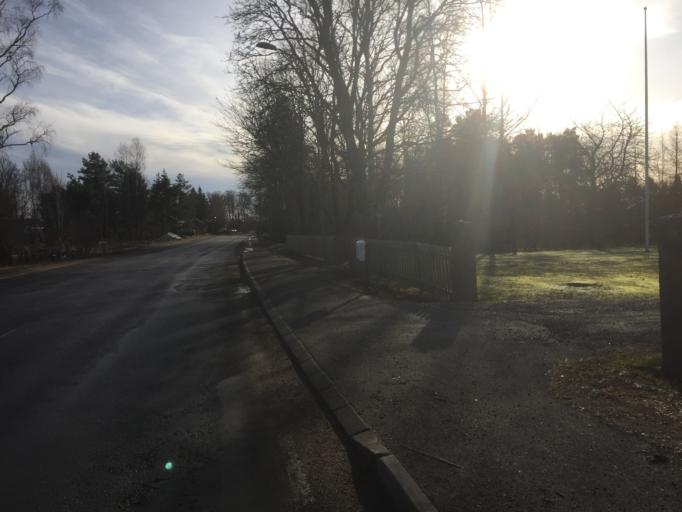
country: SE
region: Joenkoeping
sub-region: Aneby Kommun
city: Aneby
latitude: 57.8451
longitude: 14.8009
